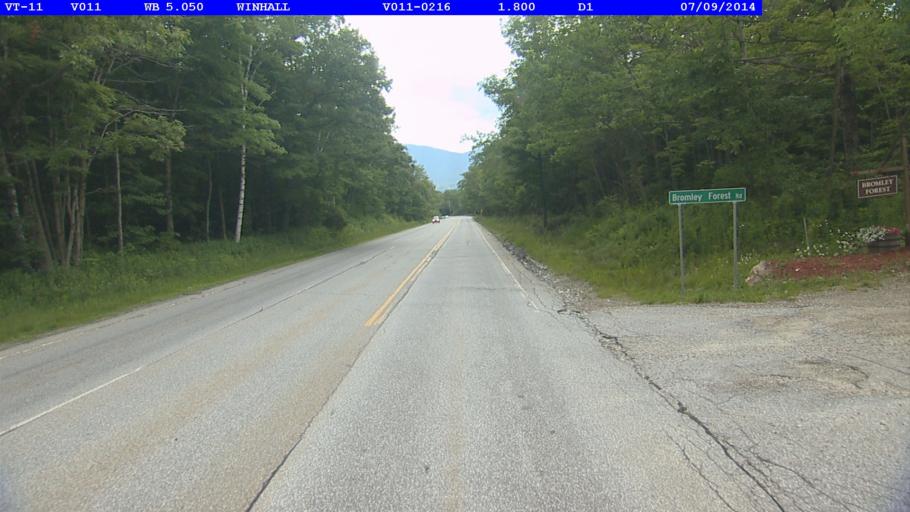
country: US
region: Vermont
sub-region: Bennington County
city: Manchester Center
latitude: 43.2069
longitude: -72.9855
